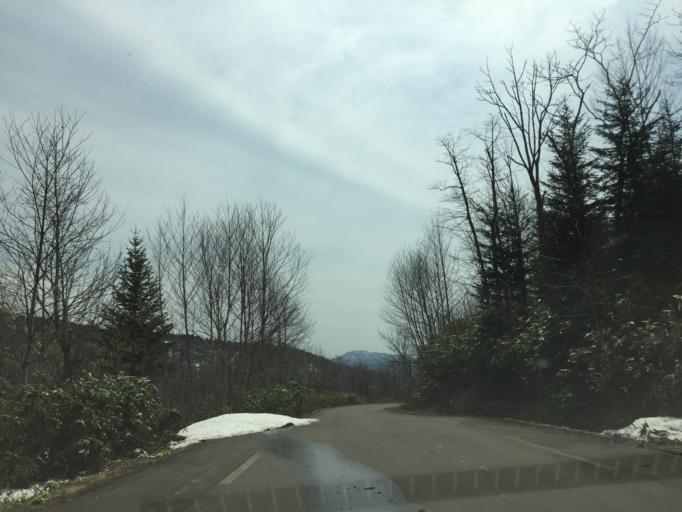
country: JP
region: Hokkaido
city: Akabira
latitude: 43.6003
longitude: 142.0653
